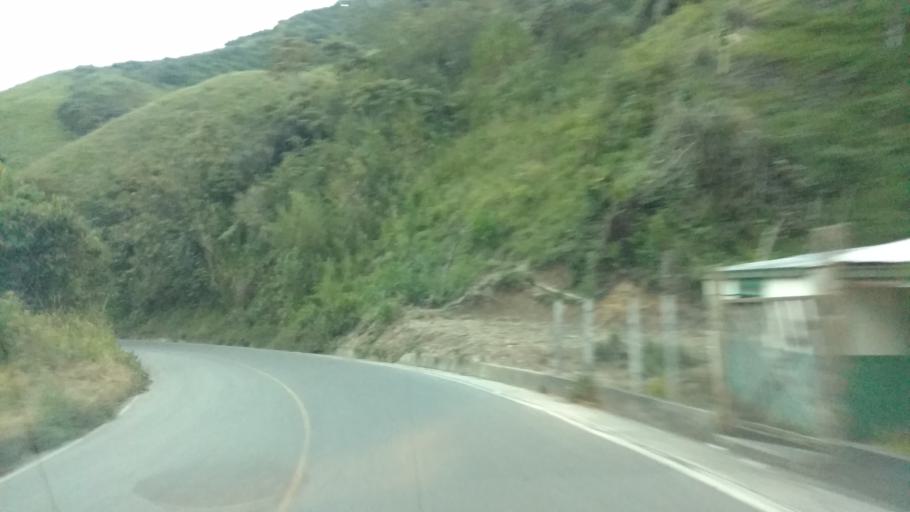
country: CO
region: Caldas
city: Aranzazu
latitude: 5.2638
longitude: -75.5004
